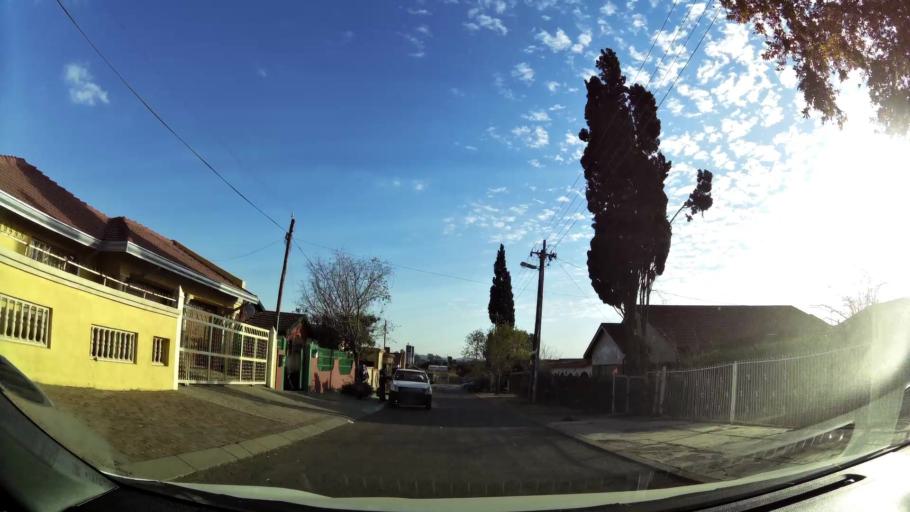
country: ZA
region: Gauteng
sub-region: City of Tshwane Metropolitan Municipality
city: Cullinan
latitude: -25.7148
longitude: 28.3725
